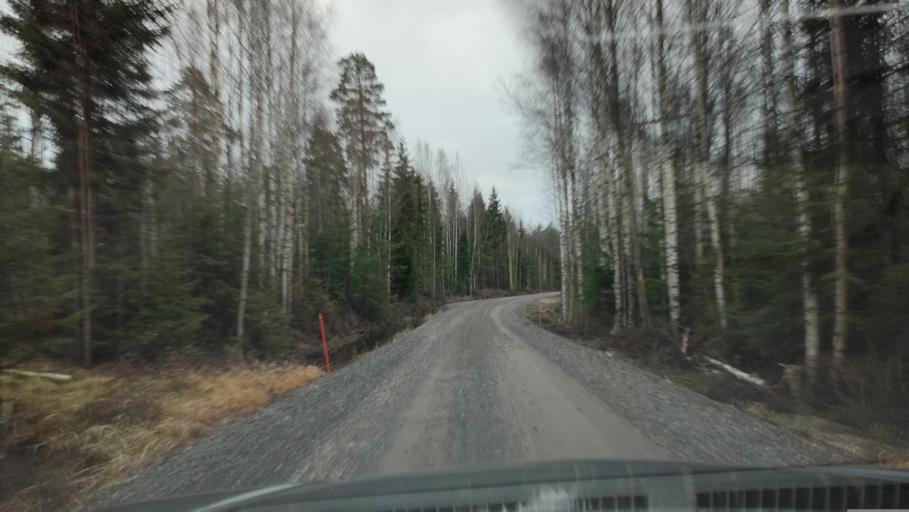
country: FI
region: Southern Ostrobothnia
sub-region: Suupohja
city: Karijoki
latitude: 62.2142
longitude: 21.6021
